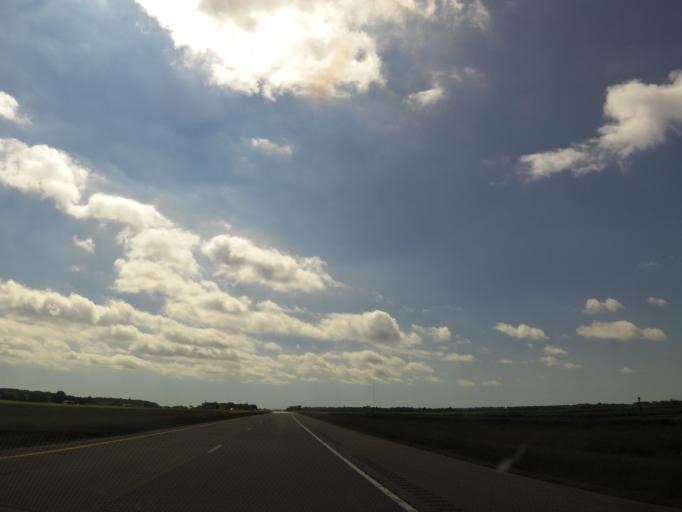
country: US
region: Minnesota
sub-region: Polk County
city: East Grand Forks
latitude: 47.8361
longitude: -96.8376
